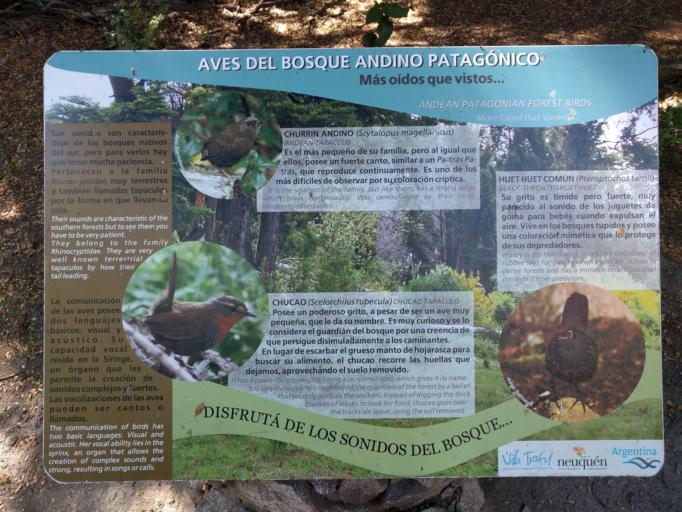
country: AR
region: Neuquen
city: Villa La Angostura
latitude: -40.6586
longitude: -71.4057
